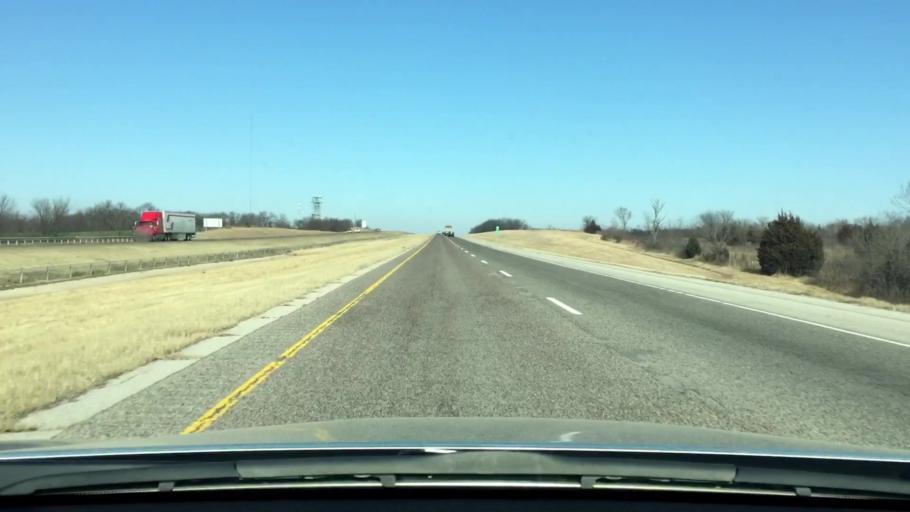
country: US
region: Oklahoma
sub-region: McClain County
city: Purcell
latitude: 34.9283
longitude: -97.3607
